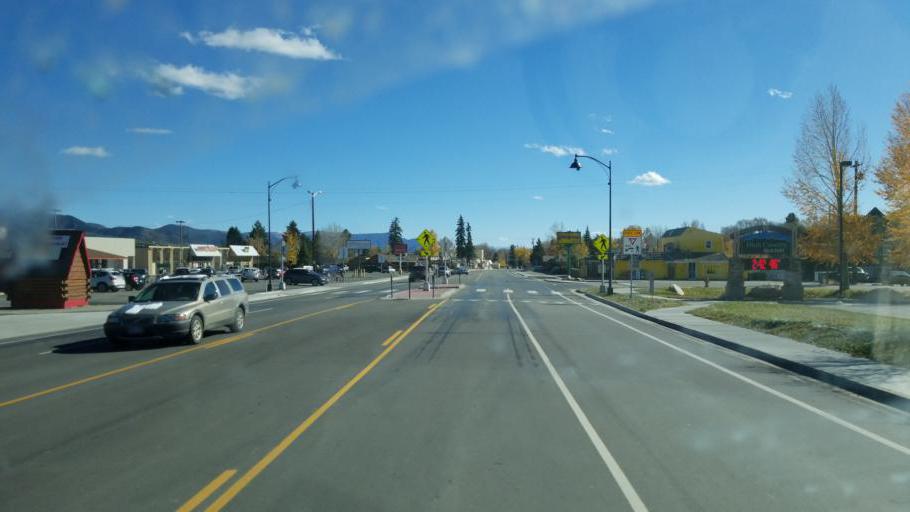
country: US
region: Colorado
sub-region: Chaffee County
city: Buena Vista
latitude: 38.8458
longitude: -106.1349
